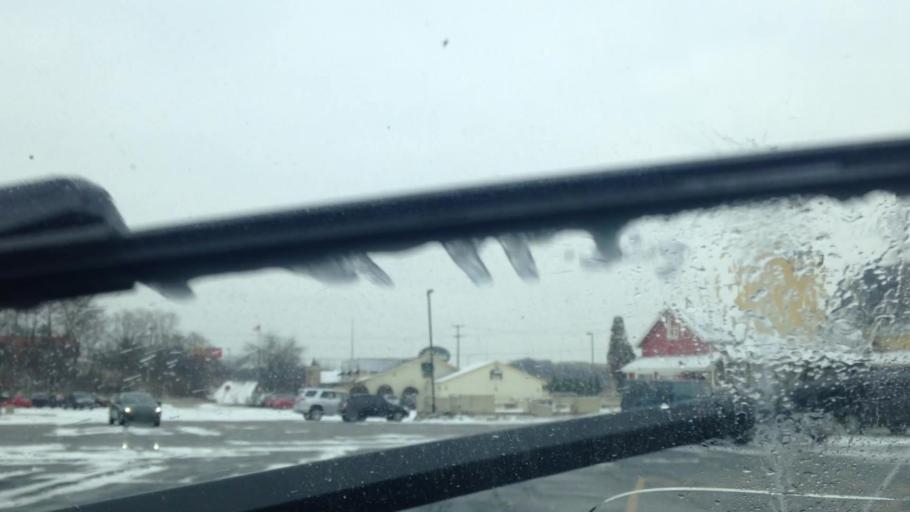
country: US
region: Wisconsin
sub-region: Waukesha County
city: Delafield
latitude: 43.0531
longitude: -88.3778
